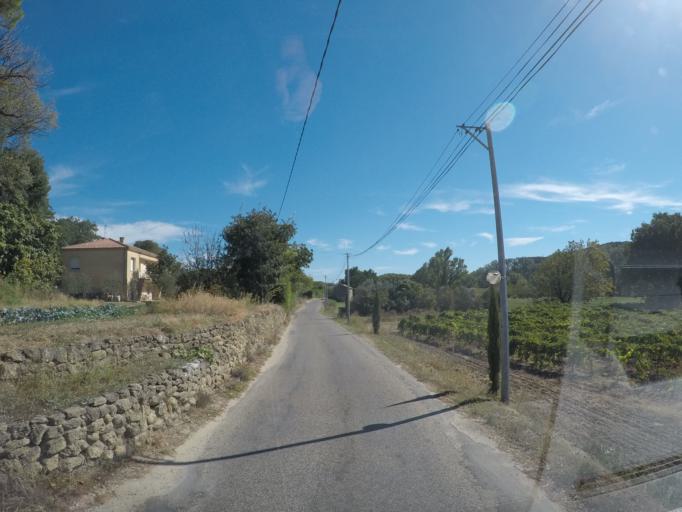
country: FR
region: Rhone-Alpes
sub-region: Departement de la Drome
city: Suze-la-Rousse
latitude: 44.2941
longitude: 4.8300
